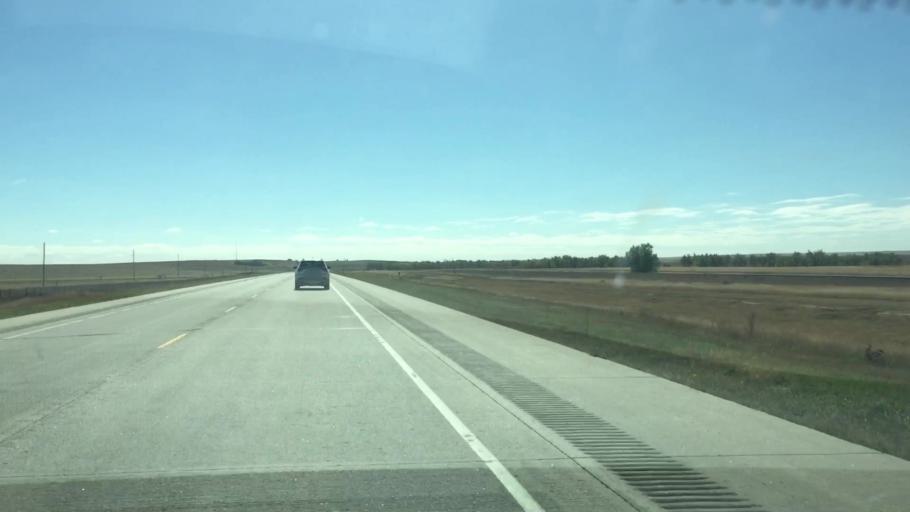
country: US
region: Colorado
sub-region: Lincoln County
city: Limon
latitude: 39.2313
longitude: -103.6169
